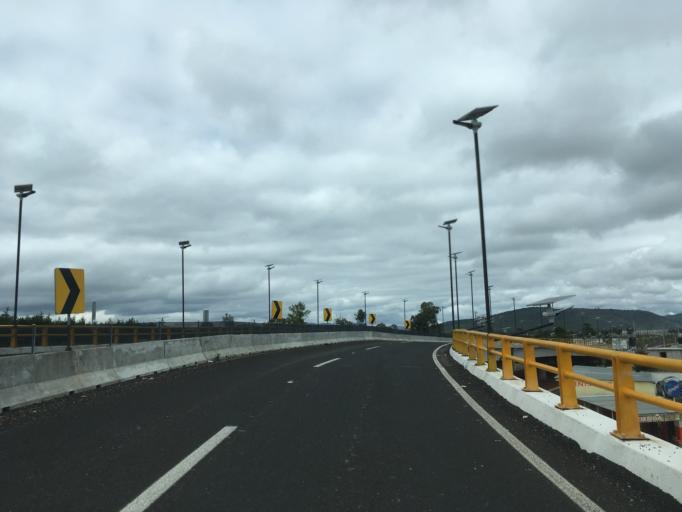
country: MX
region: Hidalgo
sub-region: Atotonilco el Grande
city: La Estancia
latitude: 20.2976
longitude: -98.6779
